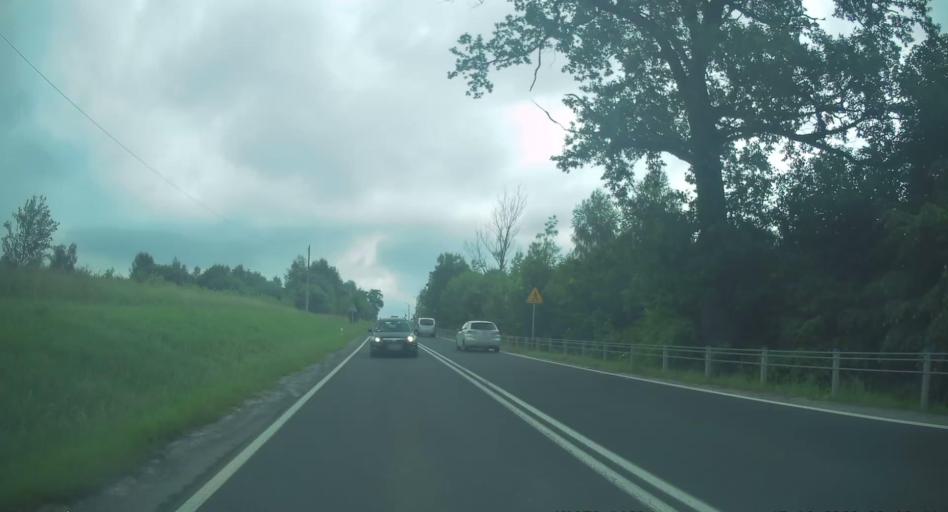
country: PL
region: Lesser Poland Voivodeship
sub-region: Powiat wadowicki
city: Kalwaria Zebrzydowska
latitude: 49.8699
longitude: 19.6495
